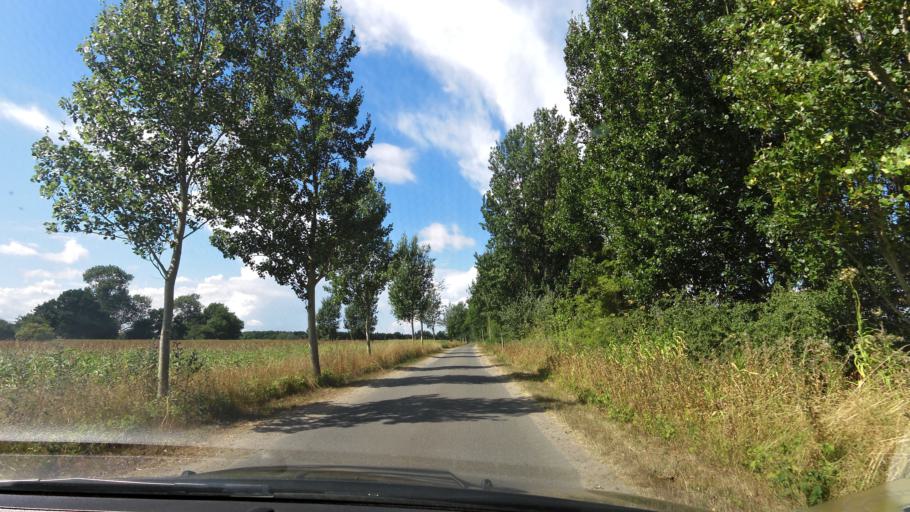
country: DK
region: South Denmark
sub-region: Nordfyns Kommune
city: Otterup
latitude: 55.5437
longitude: 10.4687
